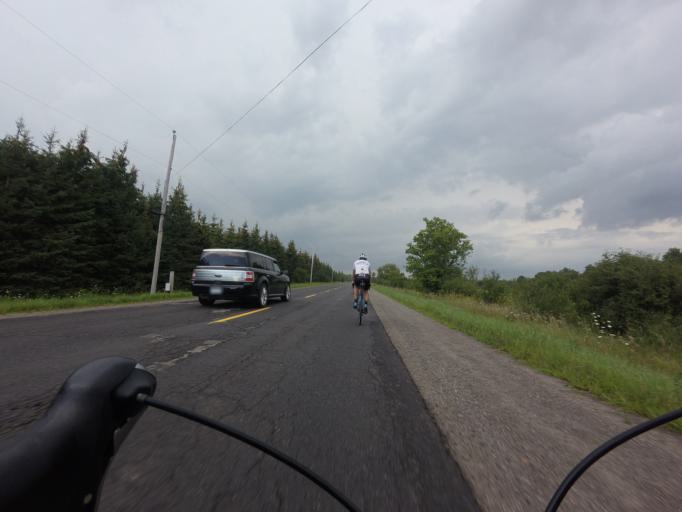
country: CA
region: Ontario
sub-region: Lanark County
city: Smiths Falls
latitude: 44.8812
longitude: -75.8161
